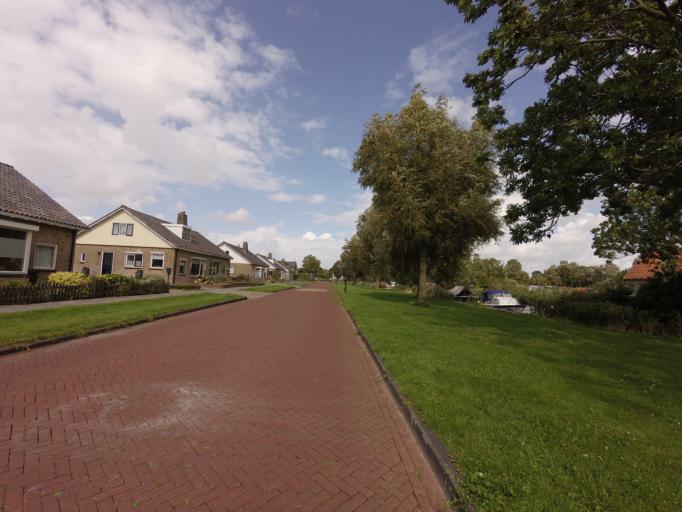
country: NL
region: Friesland
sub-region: Gemeente Franekeradeel
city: Franeker
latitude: 53.1892
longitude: 5.5459
